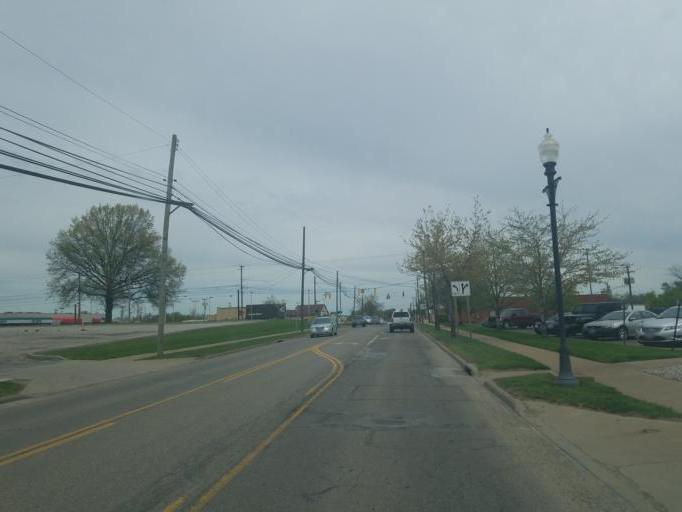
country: US
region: Ohio
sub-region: Wayne County
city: Orrville
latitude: 40.8526
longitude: -81.7639
